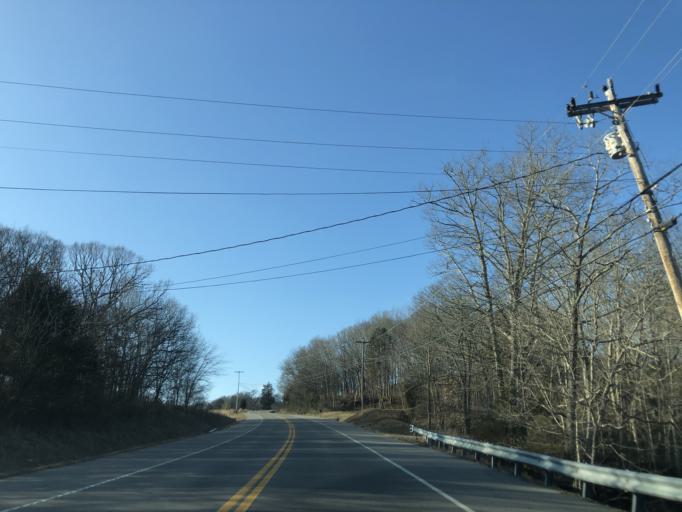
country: US
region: Tennessee
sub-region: Sumner County
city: White House
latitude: 36.4672
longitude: -86.5621
